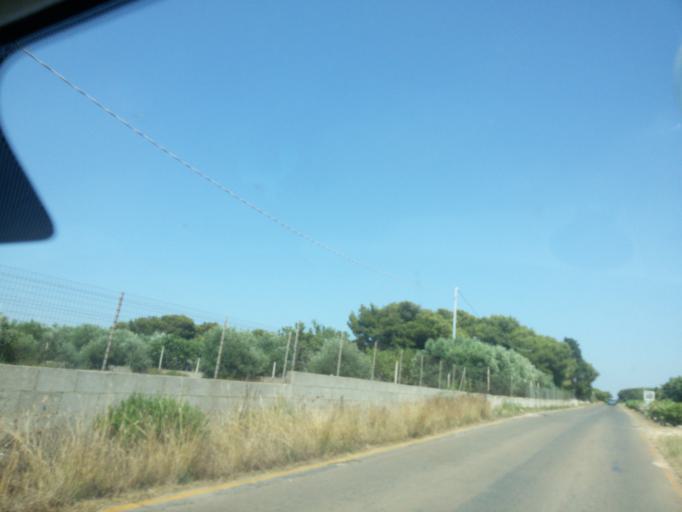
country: IT
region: Apulia
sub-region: Provincia di Lecce
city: Nardo
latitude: 40.1741
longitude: 17.9502
